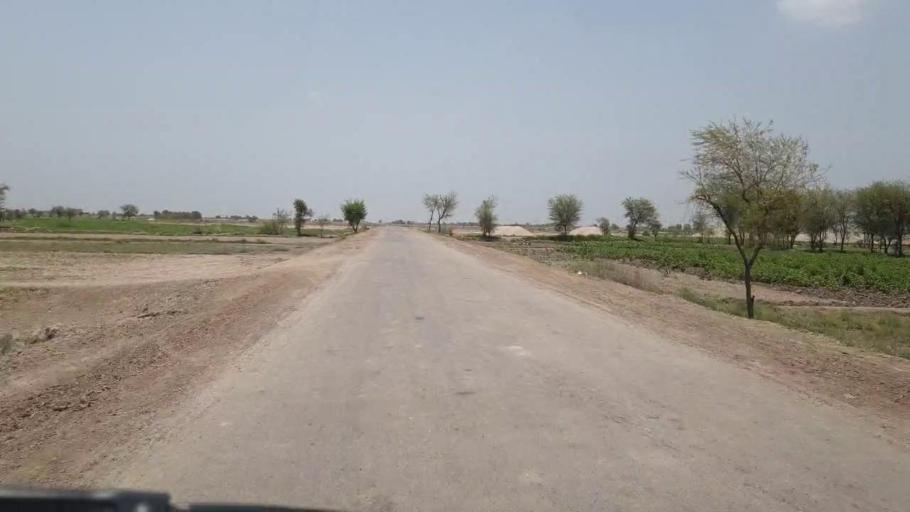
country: PK
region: Sindh
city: Daulatpur
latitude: 26.4465
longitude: 68.1163
